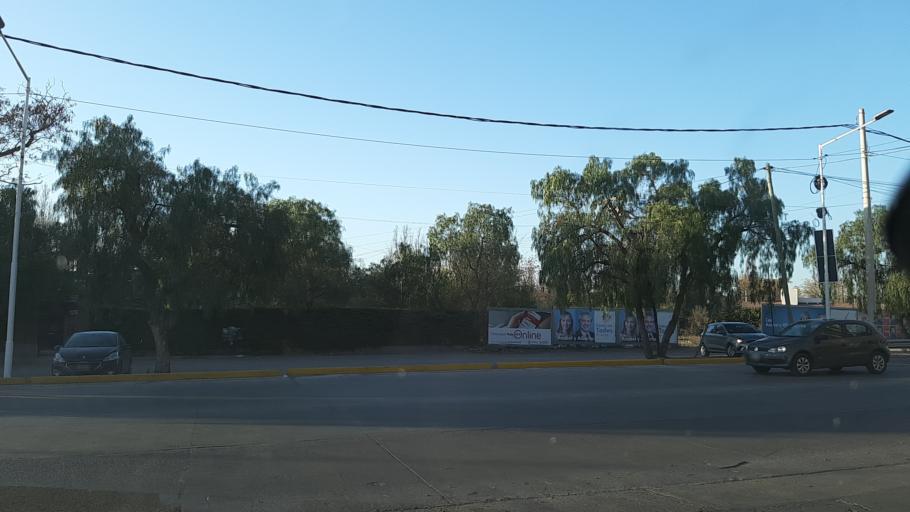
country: AR
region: Mendoza
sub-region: Departamento de Godoy Cruz
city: Godoy Cruz
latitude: -32.9615
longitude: -68.8673
